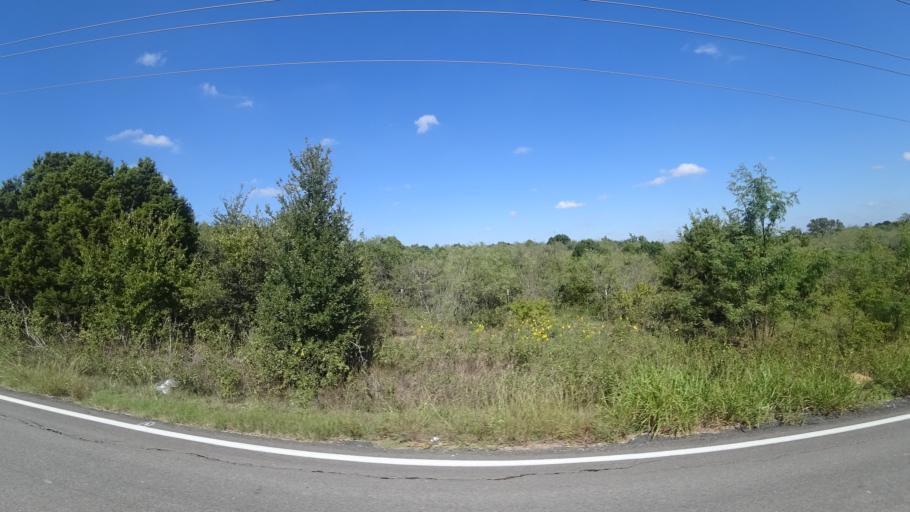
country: US
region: Texas
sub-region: Travis County
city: Manor
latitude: 30.3515
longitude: -97.6348
